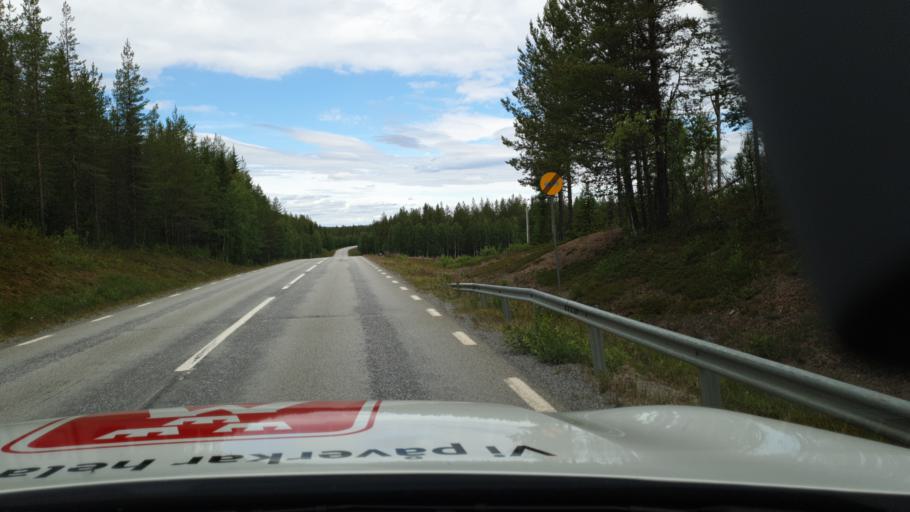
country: SE
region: Vaesterbotten
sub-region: Storumans Kommun
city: Fristad
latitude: 65.3104
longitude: 16.7000
